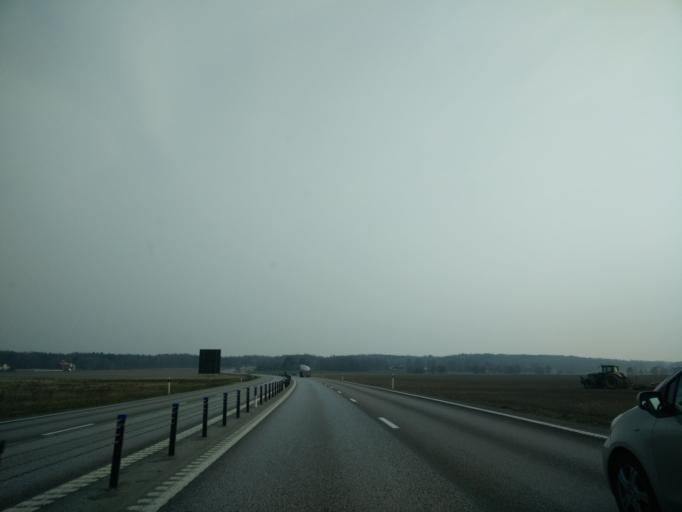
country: SE
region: Vaermland
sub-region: Karlstads Kommun
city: Karlstad
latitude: 59.4212
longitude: 13.4096
